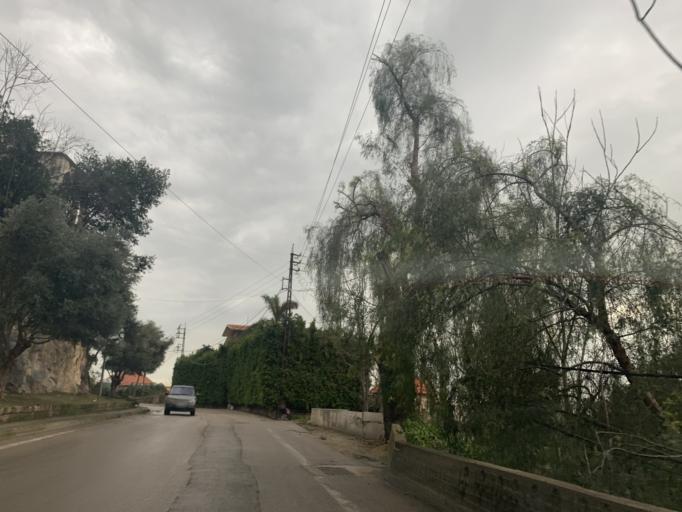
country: LB
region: Mont-Liban
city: Djounie
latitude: 33.9831
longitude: 35.6251
